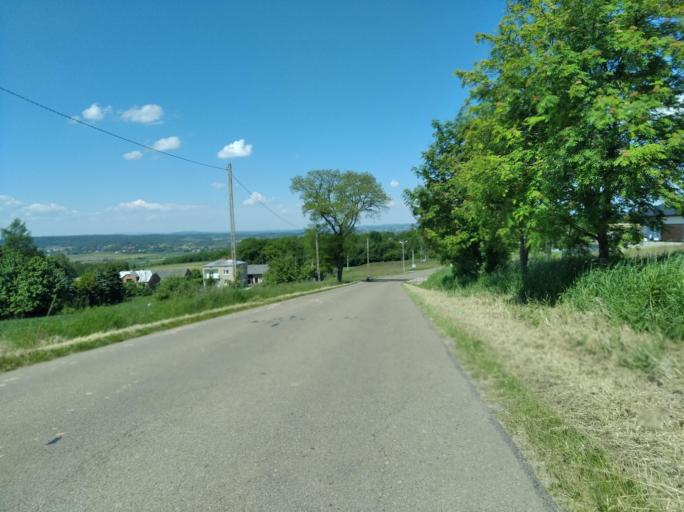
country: PL
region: Subcarpathian Voivodeship
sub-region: Powiat jasielski
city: Tarnowiec
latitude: 49.7215
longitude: 21.5971
